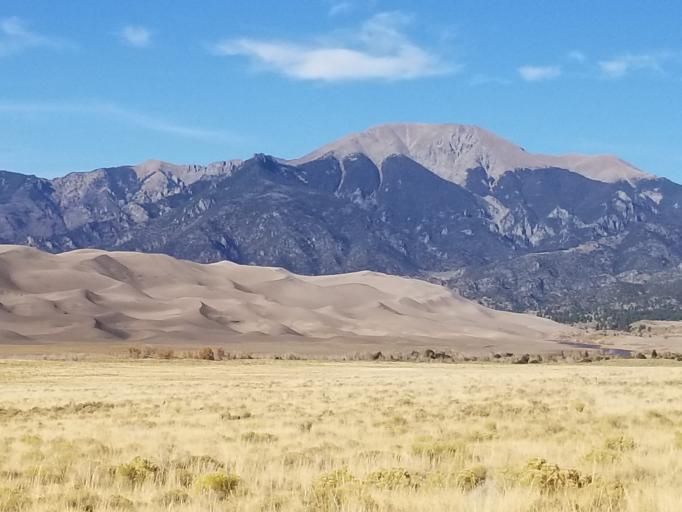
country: US
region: Colorado
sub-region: Alamosa County
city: Alamosa East
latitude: 37.7203
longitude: -105.5234
